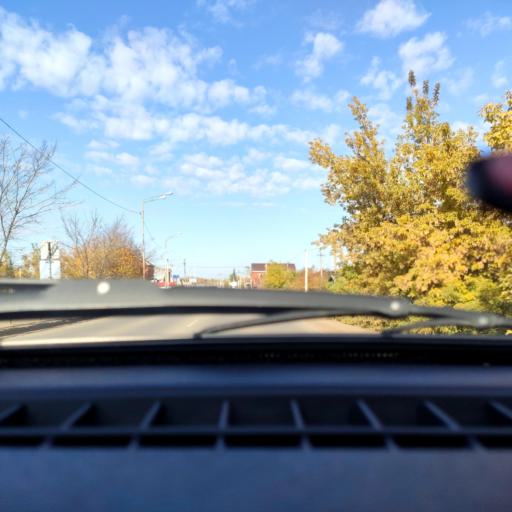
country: RU
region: Bashkortostan
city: Ufa
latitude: 54.6116
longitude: 55.9386
